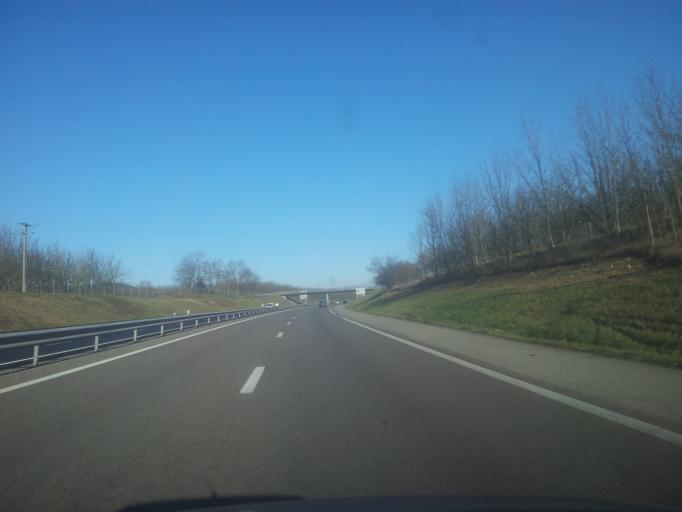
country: FR
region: Rhone-Alpes
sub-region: Departement de l'Isere
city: Vinay
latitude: 45.1825
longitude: 5.4029
